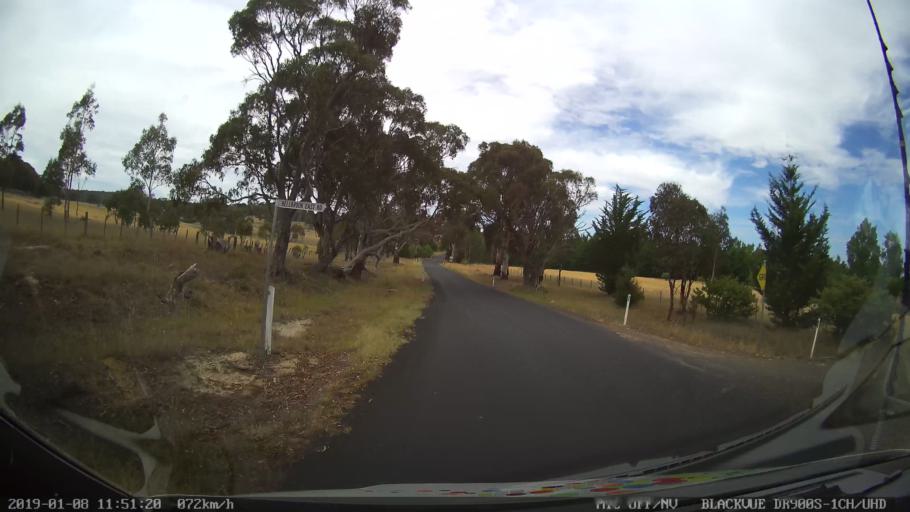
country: AU
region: New South Wales
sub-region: Armidale Dumaresq
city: Armidale
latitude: -30.3920
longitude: 151.5594
